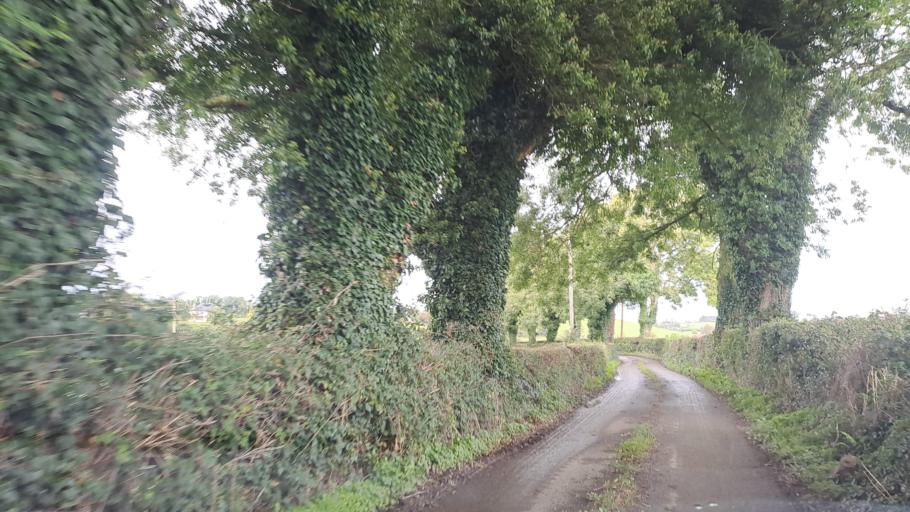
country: IE
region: Ulster
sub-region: County Monaghan
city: Carrickmacross
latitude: 53.9600
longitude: -6.7549
